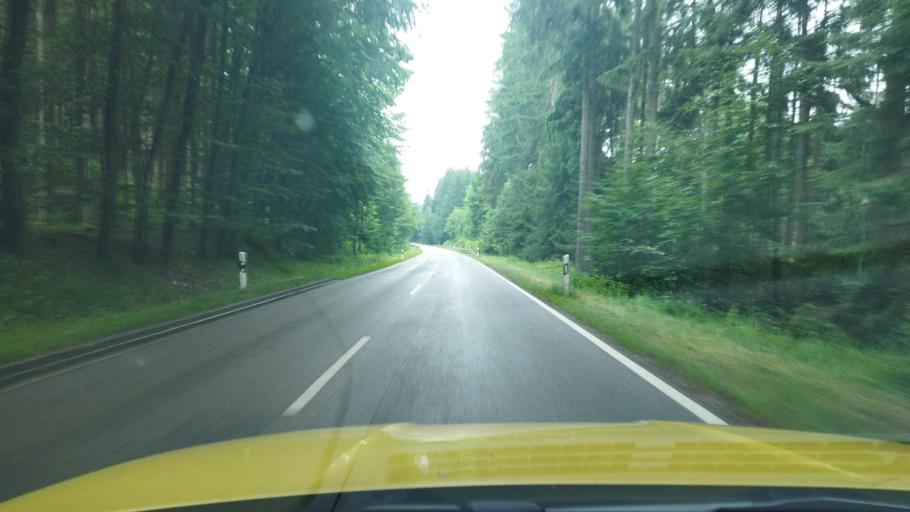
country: DE
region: Bavaria
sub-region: Regierungsbezirk Mittelfranken
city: Hottingen
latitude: 49.0889
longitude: 11.0049
